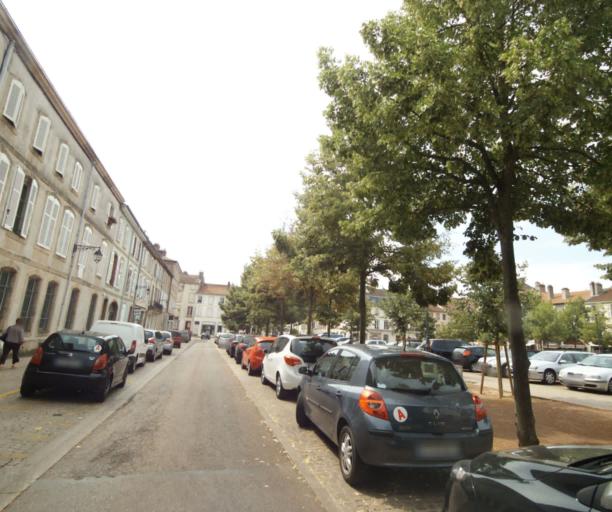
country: FR
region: Lorraine
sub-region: Departement de Meurthe-et-Moselle
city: Luneville
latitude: 48.5916
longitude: 6.4957
